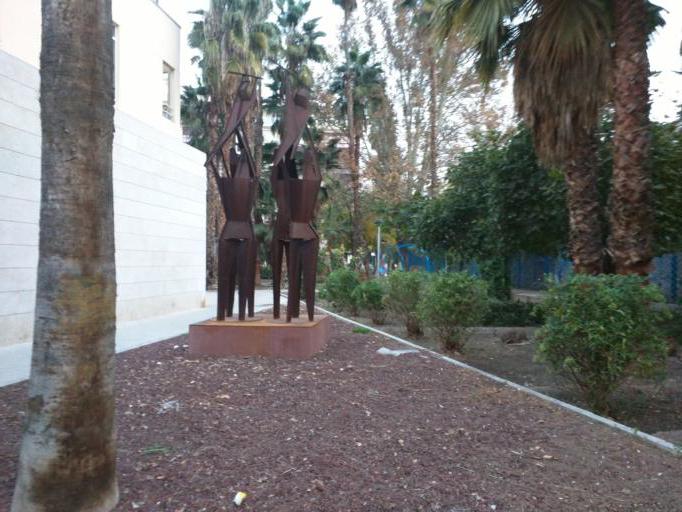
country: ES
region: Murcia
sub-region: Murcia
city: Murcia
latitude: 37.9882
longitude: -1.1375
